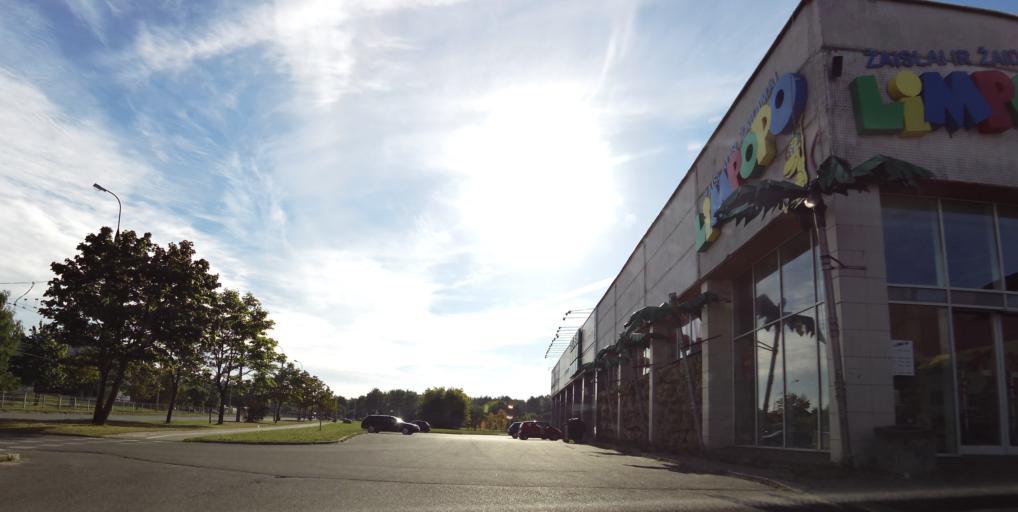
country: LT
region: Vilnius County
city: Justiniskes
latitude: 54.7034
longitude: 25.2201
